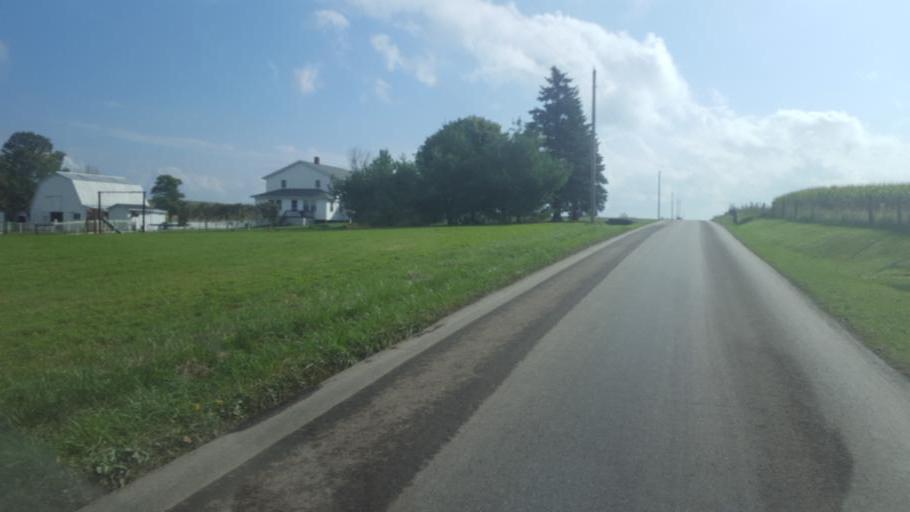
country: US
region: Ohio
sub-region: Holmes County
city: Millersburg
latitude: 40.6410
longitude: -81.8614
